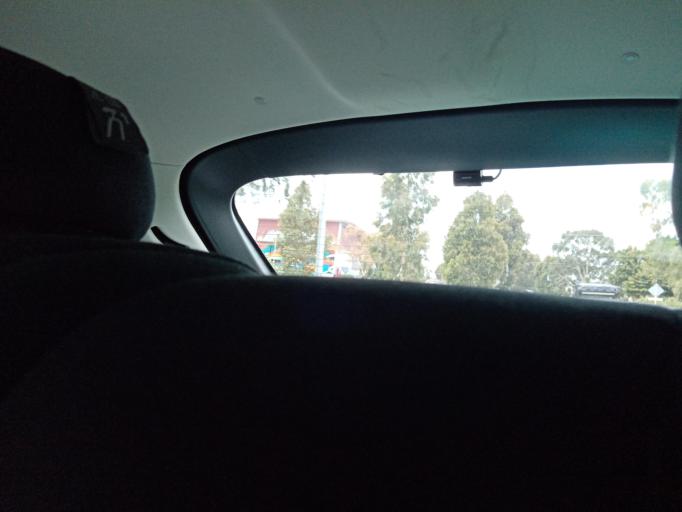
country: AU
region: Western Australia
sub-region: City of Cockburn
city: Success
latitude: -32.1302
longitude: 115.8526
